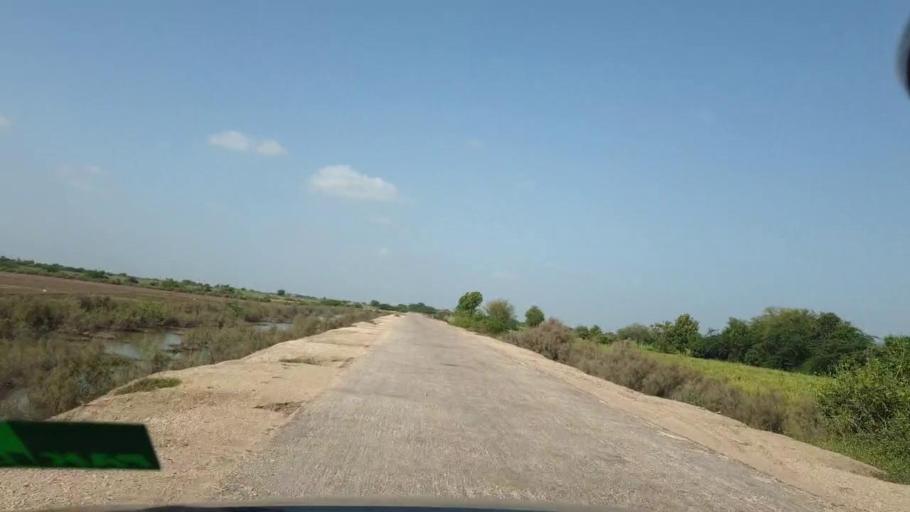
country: PK
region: Sindh
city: Tando Bago
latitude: 24.6919
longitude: 69.1890
